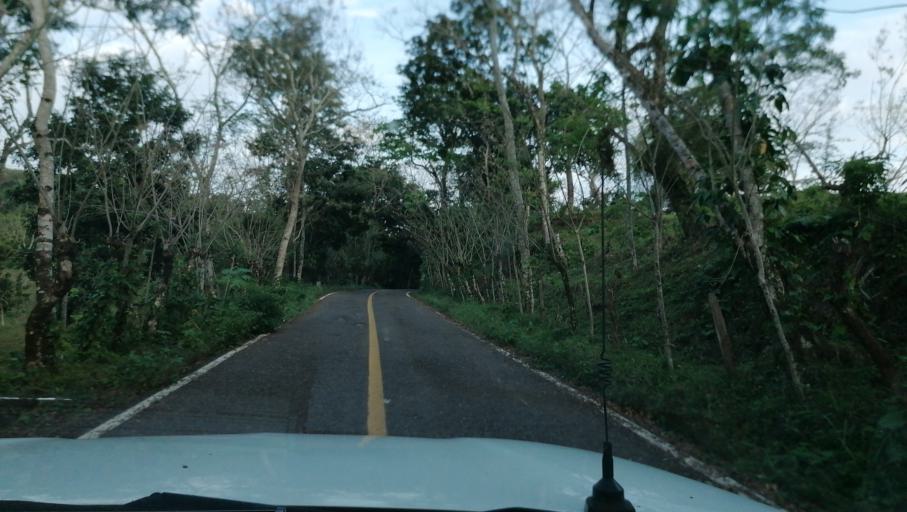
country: MX
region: Chiapas
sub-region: Juarez
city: El Triunfo 1ra. Seccion (Cardona)
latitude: 17.5012
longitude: -93.2396
